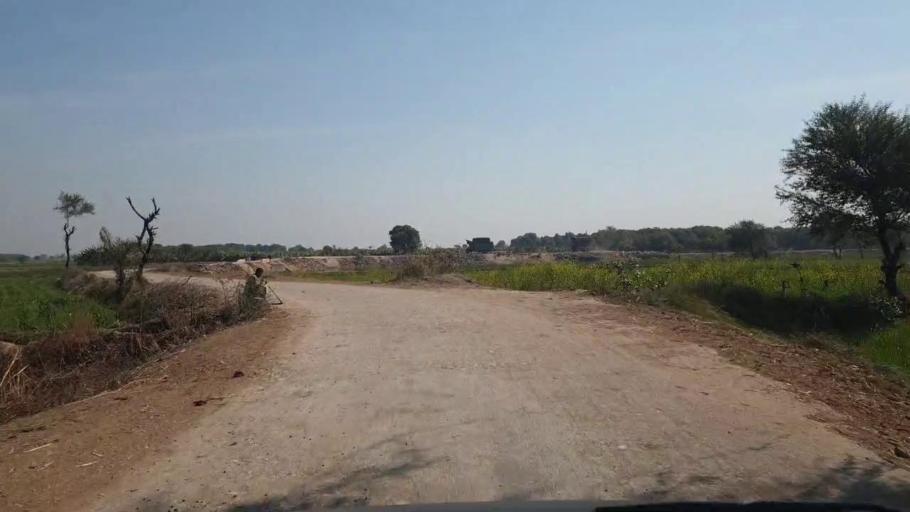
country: PK
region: Sindh
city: Chambar
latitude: 25.3863
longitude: 68.7836
